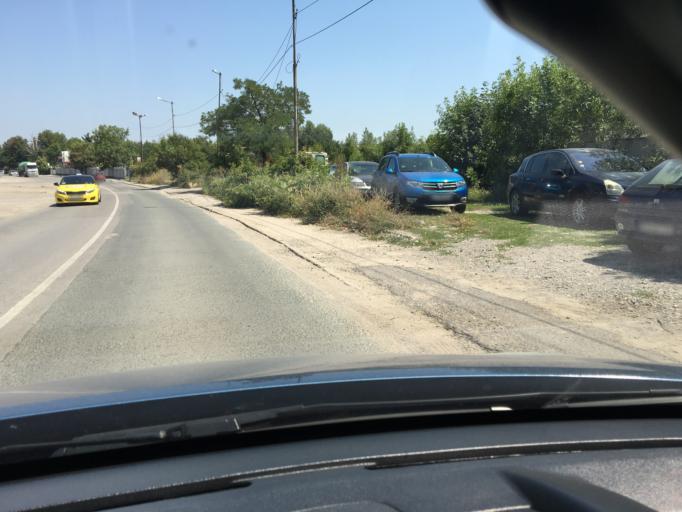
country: BG
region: Sofia-Capital
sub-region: Stolichna Obshtina
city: Sofia
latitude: 42.6367
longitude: 23.4005
